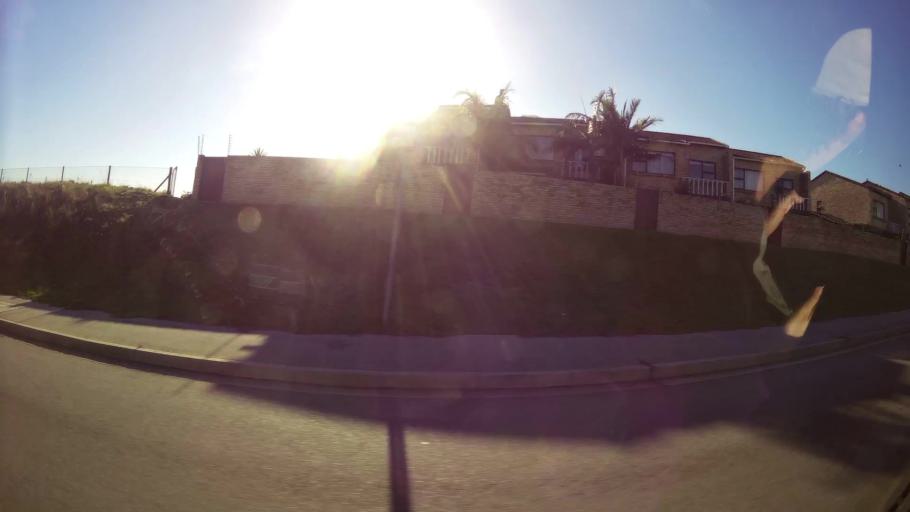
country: ZA
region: Eastern Cape
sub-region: Nelson Mandela Bay Metropolitan Municipality
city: Port Elizabeth
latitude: -33.9724
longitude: 25.6247
